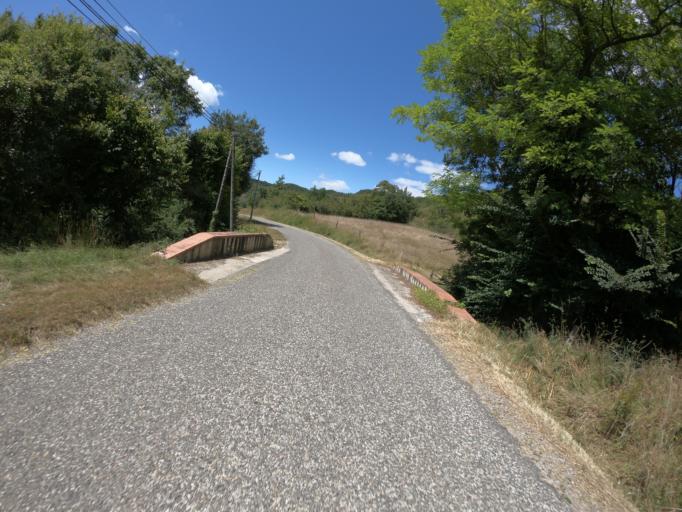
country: FR
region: Midi-Pyrenees
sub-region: Departement de l'Ariege
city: Mirepoix
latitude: 43.0518
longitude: 1.8146
